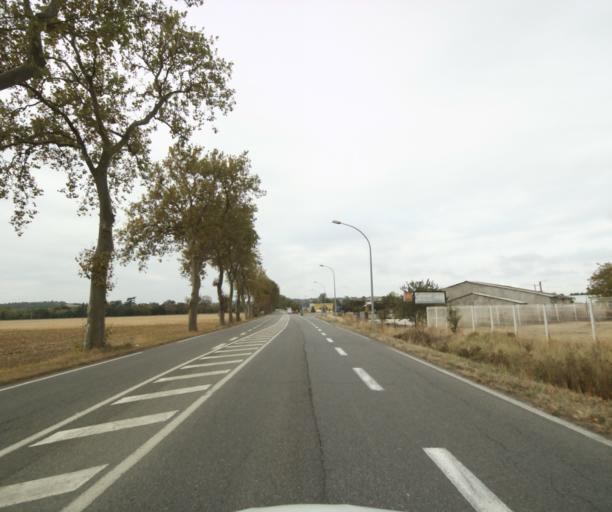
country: FR
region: Midi-Pyrenees
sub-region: Departement de la Haute-Garonne
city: Villefranche-de-Lauragais
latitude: 43.3979
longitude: 1.7066
